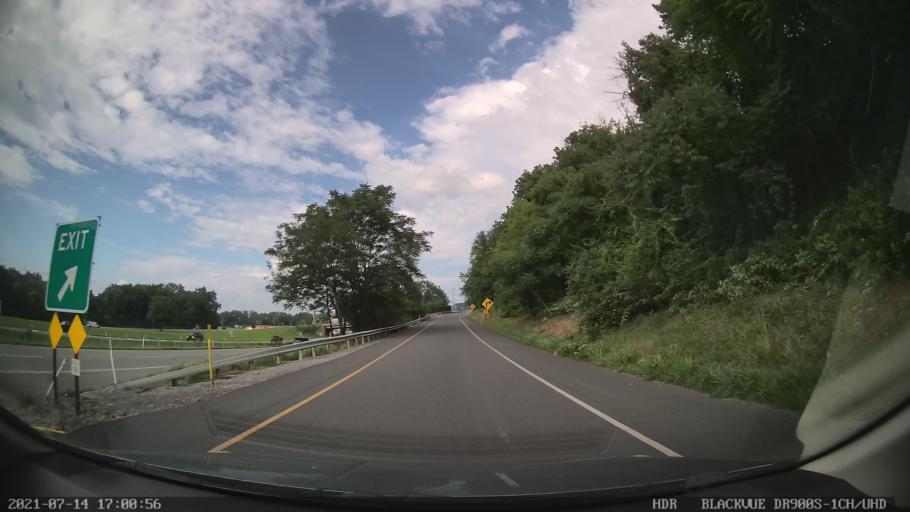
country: US
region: Pennsylvania
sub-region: Berks County
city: Temple
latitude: 40.4099
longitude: -75.9409
